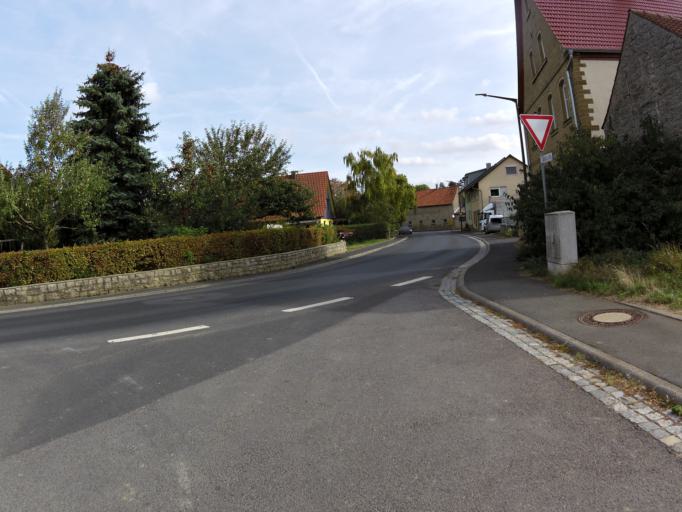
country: DE
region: Bavaria
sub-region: Regierungsbezirk Unterfranken
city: Eibelstadt
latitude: 49.6992
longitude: 9.9670
